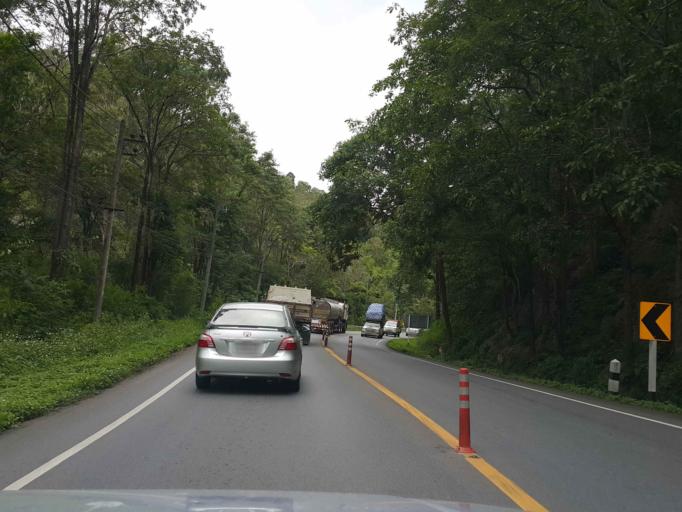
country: TH
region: Tak
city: Tak
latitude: 16.8033
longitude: 98.9563
